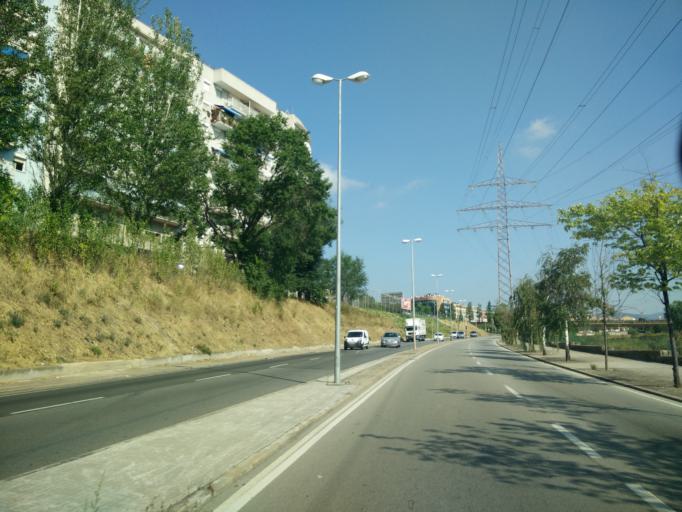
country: ES
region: Catalonia
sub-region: Provincia de Barcelona
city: Terrassa
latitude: 41.5554
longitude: 2.0352
